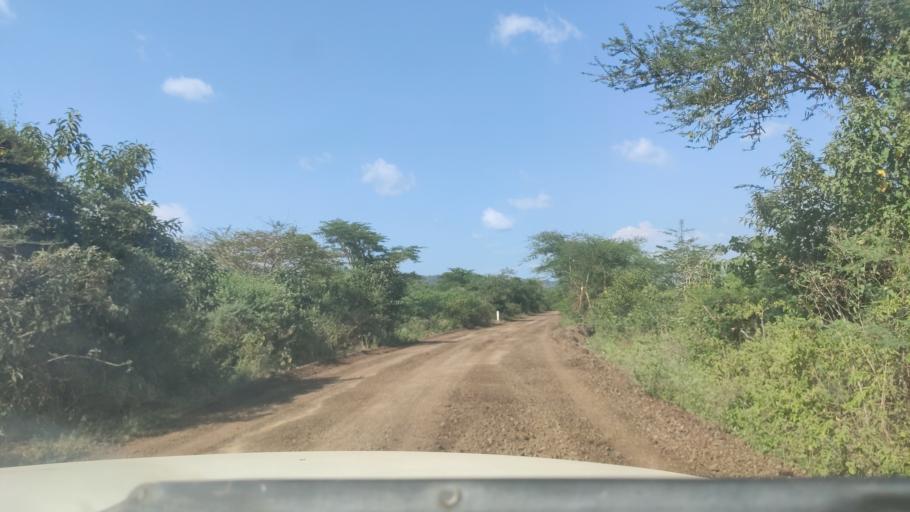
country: ET
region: Southern Nations, Nationalities, and People's Region
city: Felege Neway
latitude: 6.3766
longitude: 37.0879
